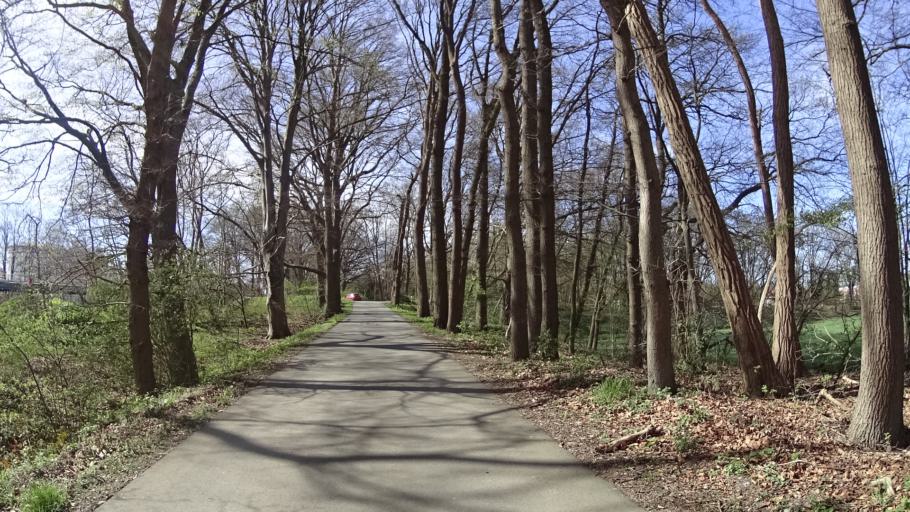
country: DE
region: Lower Saxony
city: Lingen
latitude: 52.5596
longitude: 7.2989
